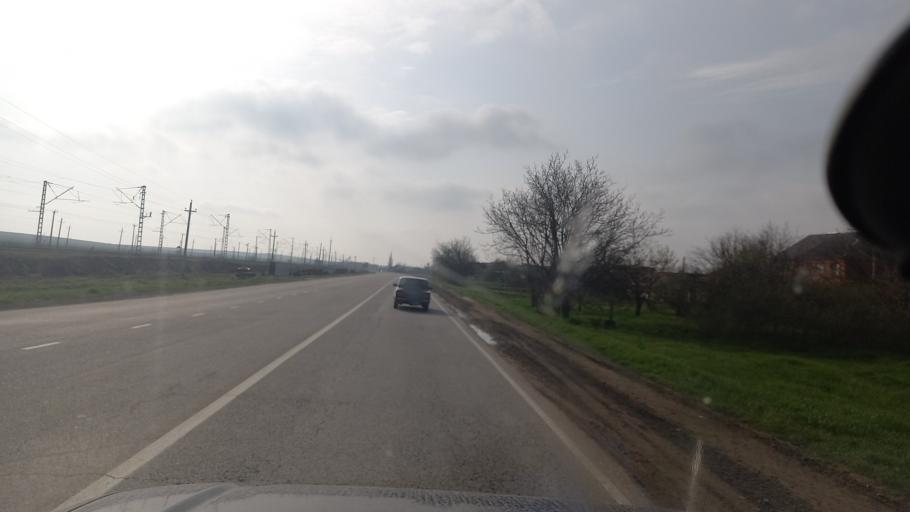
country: RU
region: Krasnodarskiy
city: Varenikovskaya
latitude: 45.1129
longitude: 37.6270
